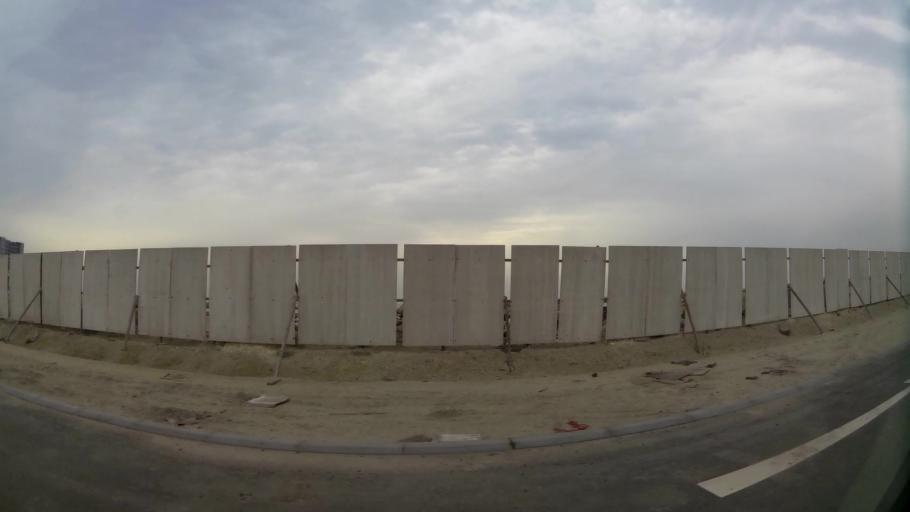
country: BH
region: Central Governorate
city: Dar Kulayb
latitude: 25.8663
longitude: 50.6060
